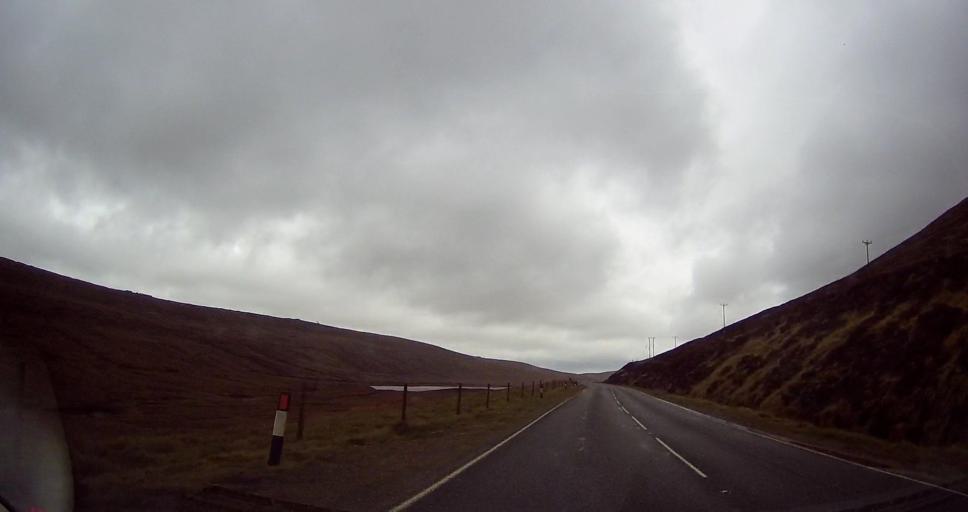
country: GB
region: Scotland
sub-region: Shetland Islands
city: Lerwick
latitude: 60.3085
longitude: -1.2445
